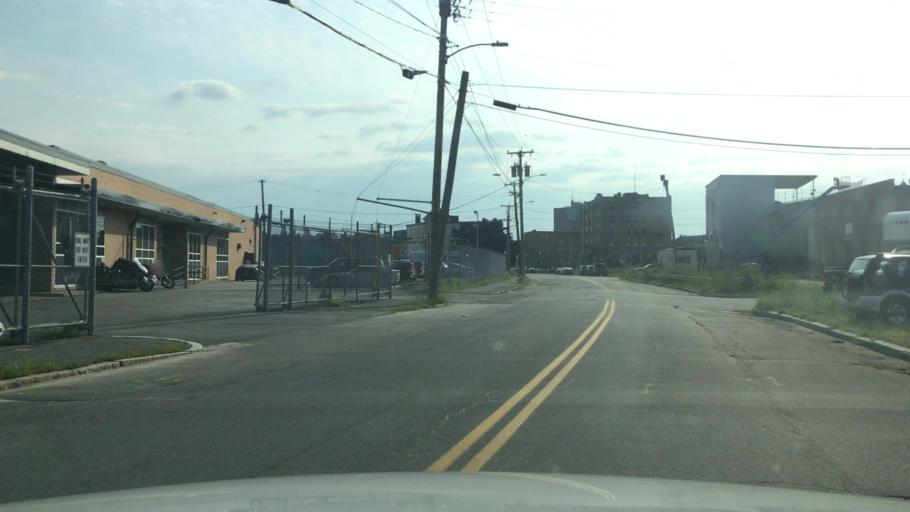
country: US
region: Maine
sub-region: Cumberland County
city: Portland
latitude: 43.6600
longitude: -70.2662
